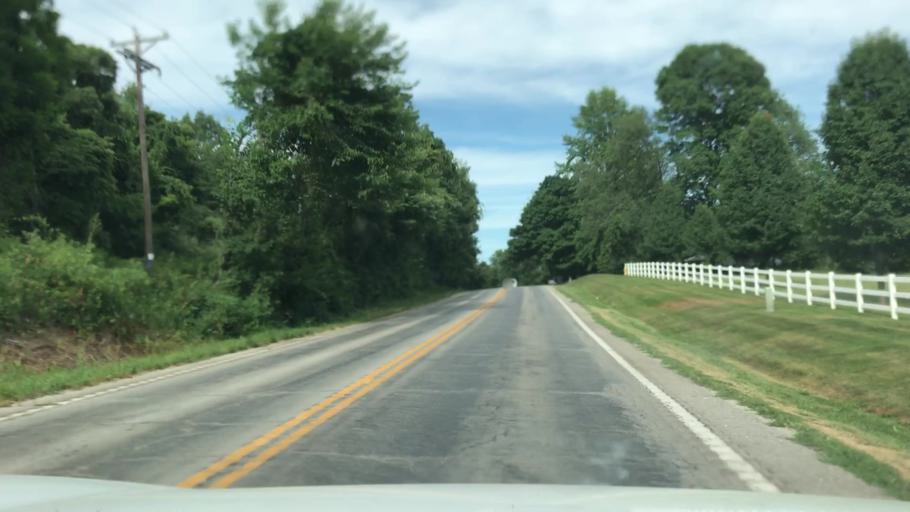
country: US
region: Missouri
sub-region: Saint Charles County
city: Weldon Spring
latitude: 38.6564
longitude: -90.7688
